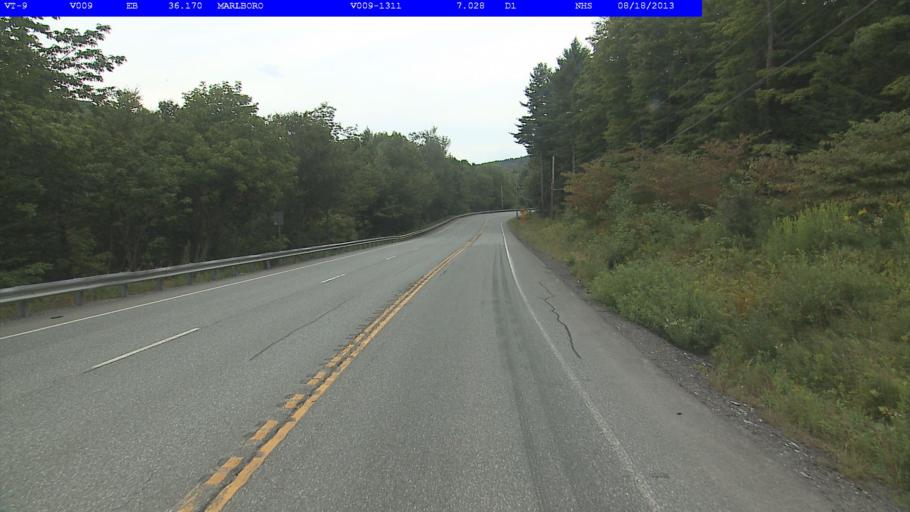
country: US
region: Vermont
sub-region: Windham County
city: West Brattleboro
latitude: 42.8801
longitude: -72.6994
